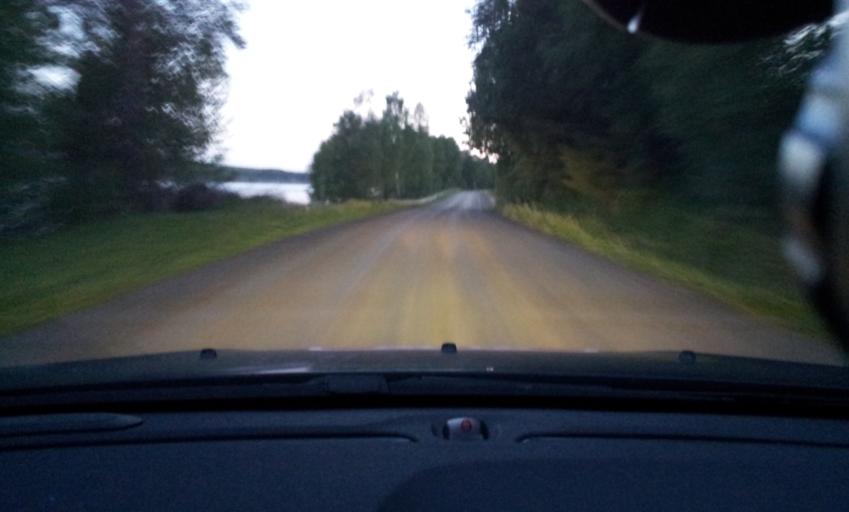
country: SE
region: Jaemtland
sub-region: Braecke Kommun
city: Braecke
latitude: 62.7171
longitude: 15.5989
